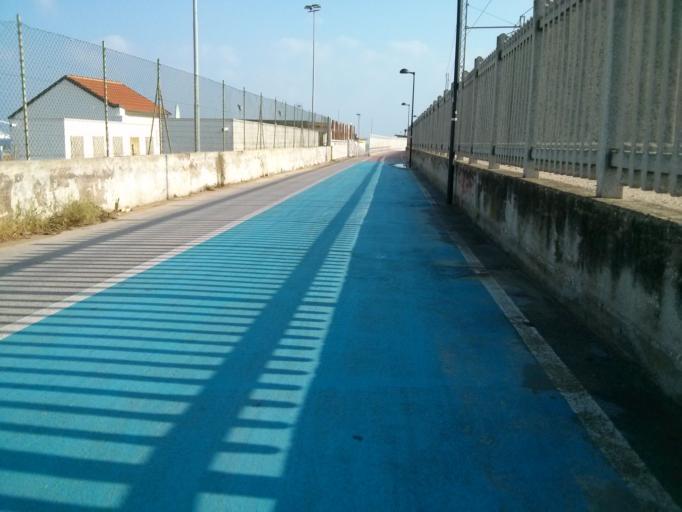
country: IT
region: The Marches
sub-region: Provincia di Pesaro e Urbino
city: Pesaro
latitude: 43.9060
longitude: 12.9290
